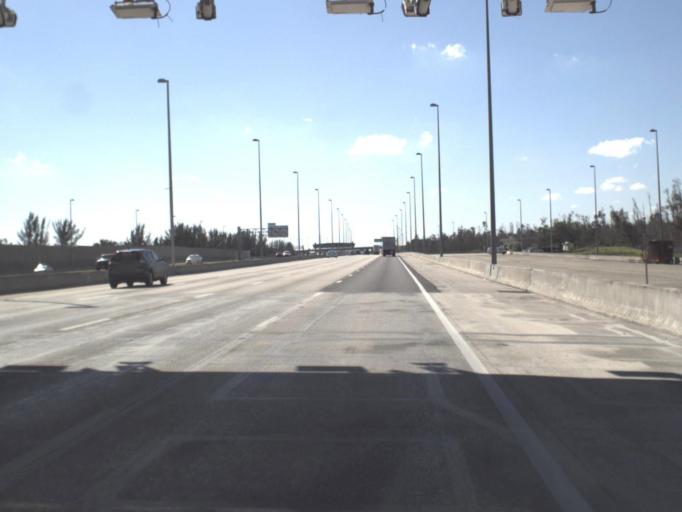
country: US
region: Florida
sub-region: Miami-Dade County
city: Doral
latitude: 25.8515
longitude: -80.3876
